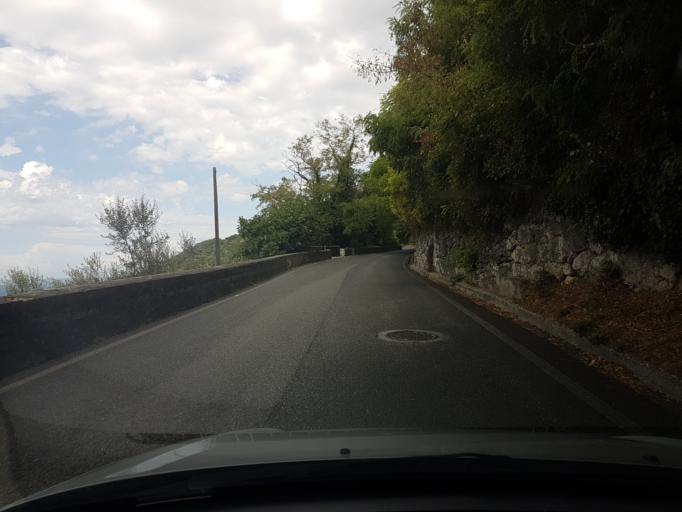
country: IT
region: Friuli Venezia Giulia
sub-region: Provincia di Trieste
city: Prosecco-Contovello
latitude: 45.6951
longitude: 13.7428
